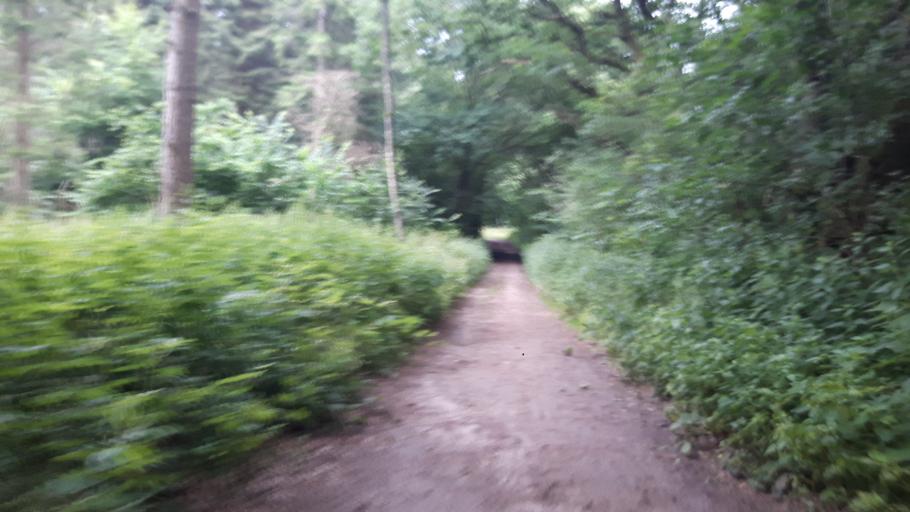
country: DE
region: Schleswig-Holstein
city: Ratekau
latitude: 53.9204
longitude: 10.7682
